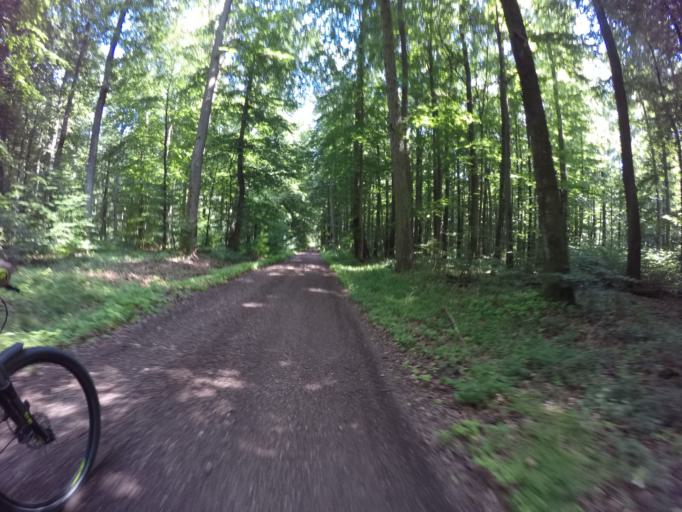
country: DE
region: Bavaria
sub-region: Lower Bavaria
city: Essing
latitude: 48.9082
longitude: 11.8029
